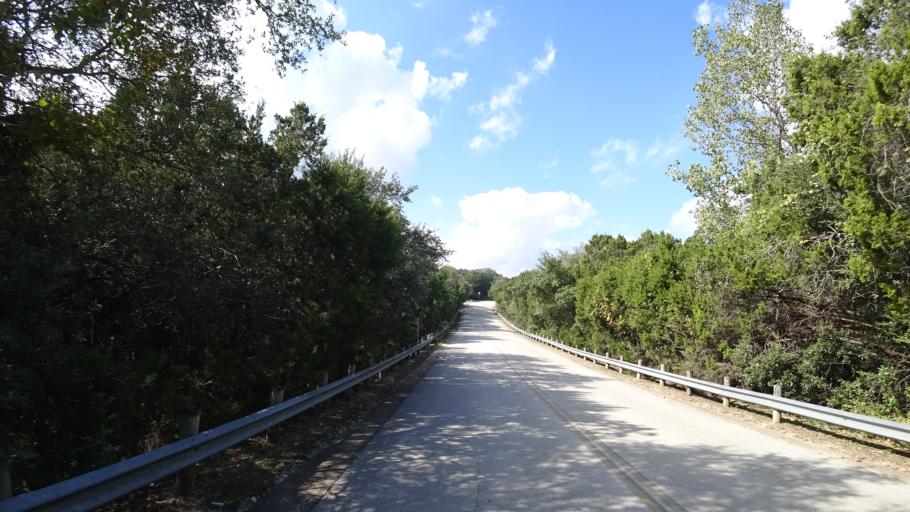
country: US
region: Texas
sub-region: Travis County
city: Barton Creek
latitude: 30.3148
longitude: -97.8733
